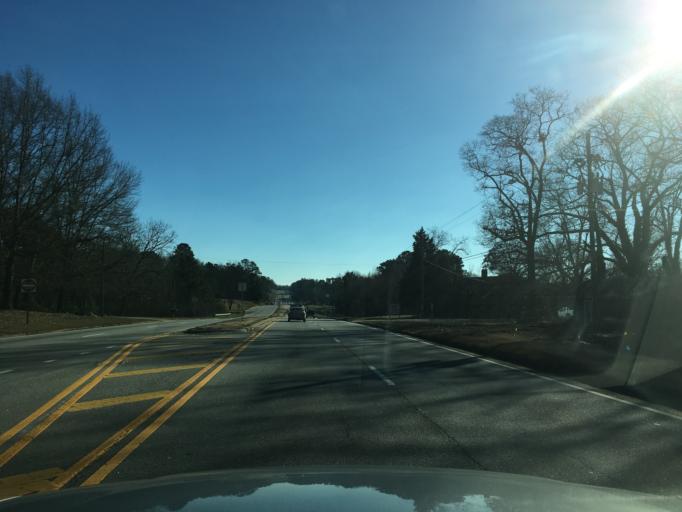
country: US
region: Georgia
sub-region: Carroll County
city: Carrollton
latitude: 33.5407
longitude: -85.0740
